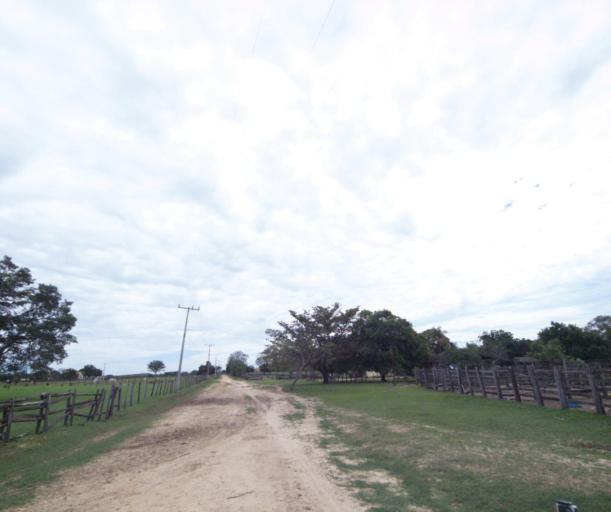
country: BR
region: Bahia
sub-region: Carinhanha
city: Carinhanha
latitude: -14.2516
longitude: -44.3531
